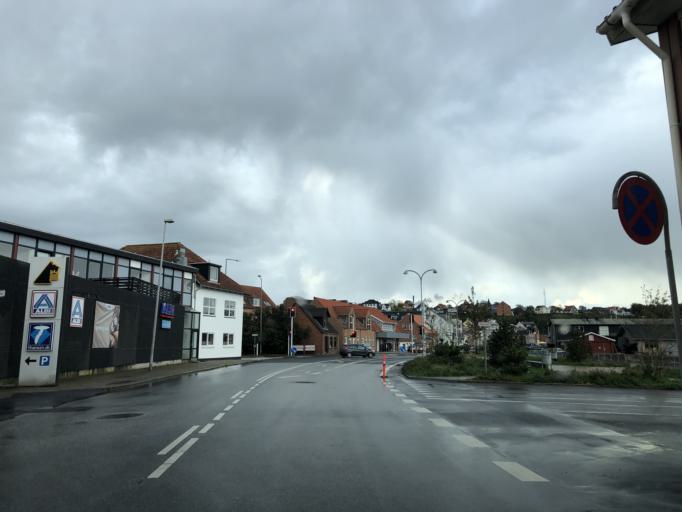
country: DK
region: Central Jutland
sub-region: Lemvig Kommune
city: Lemvig
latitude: 56.5520
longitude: 8.3101
